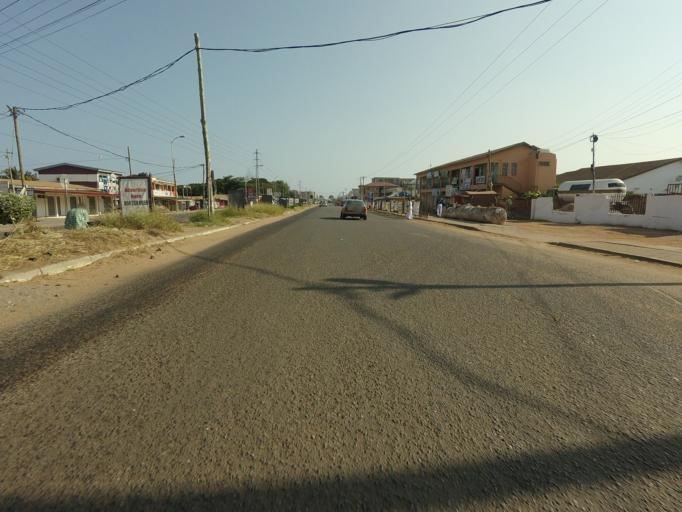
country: GH
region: Greater Accra
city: Nungua
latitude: 5.6252
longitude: -0.0686
